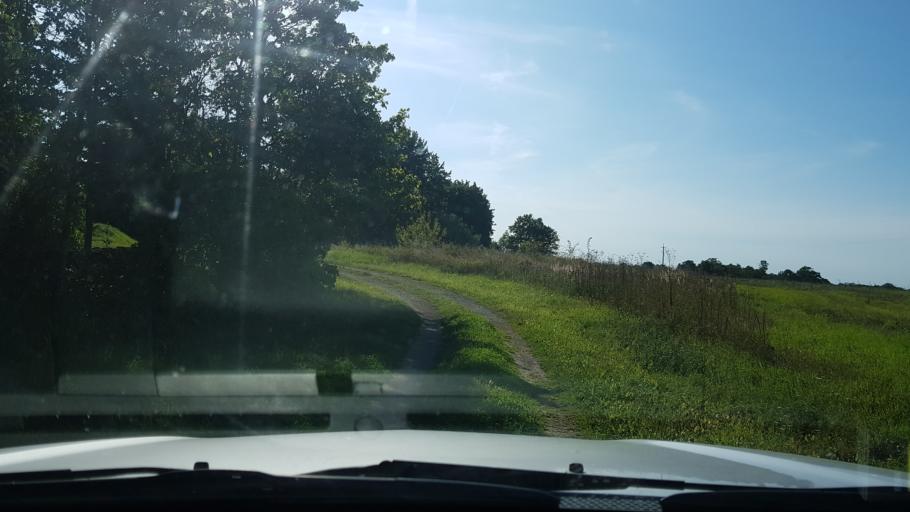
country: EE
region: Ida-Virumaa
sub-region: Narva-Joesuu linn
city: Narva-Joesuu
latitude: 59.4057
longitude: 28.0047
